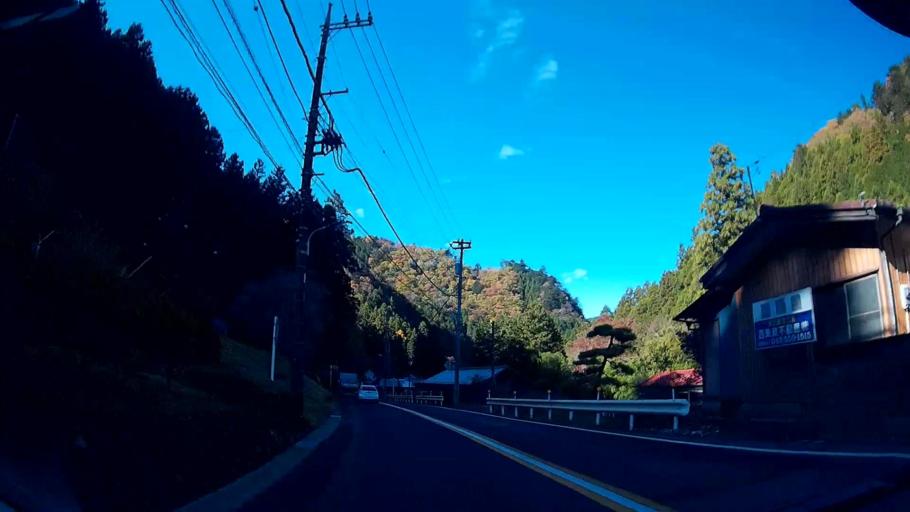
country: JP
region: Tokyo
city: Itsukaichi
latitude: 35.7235
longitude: 139.1625
